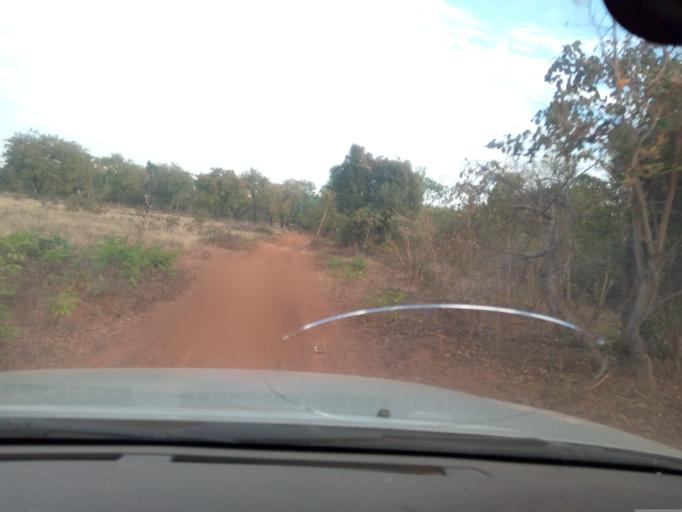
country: ML
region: Sikasso
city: Kadiolo
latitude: 10.5817
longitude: -5.8408
